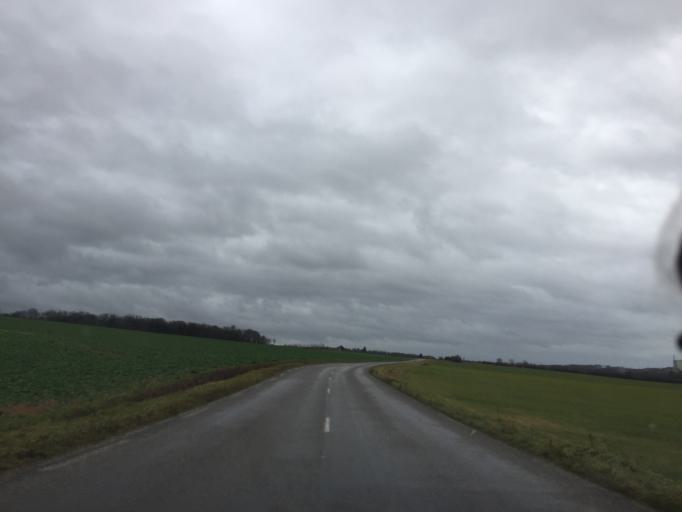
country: FR
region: Franche-Comte
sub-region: Departement du Jura
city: Dole
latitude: 47.1567
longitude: 5.5663
